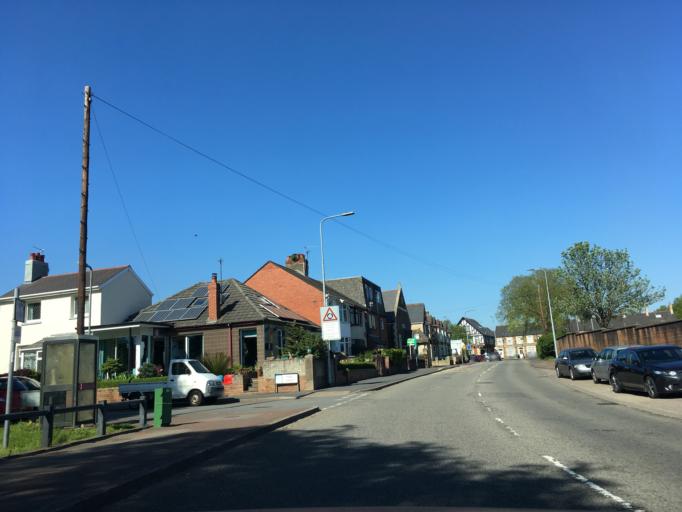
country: GB
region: Wales
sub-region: Cardiff
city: Radyr
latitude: 51.5014
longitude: -3.2275
